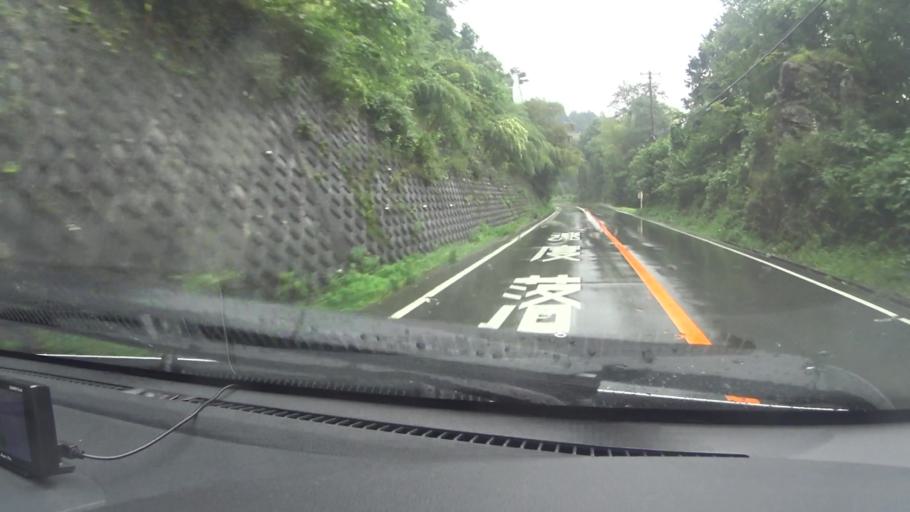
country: JP
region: Kyoto
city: Ayabe
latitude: 35.2242
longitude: 135.3368
